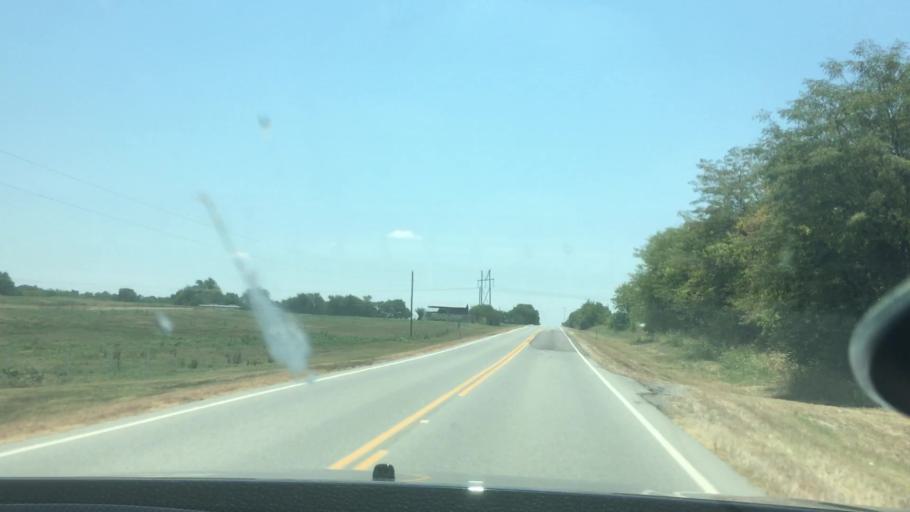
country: US
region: Oklahoma
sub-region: Coal County
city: Coalgate
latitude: 34.5240
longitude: -96.4070
